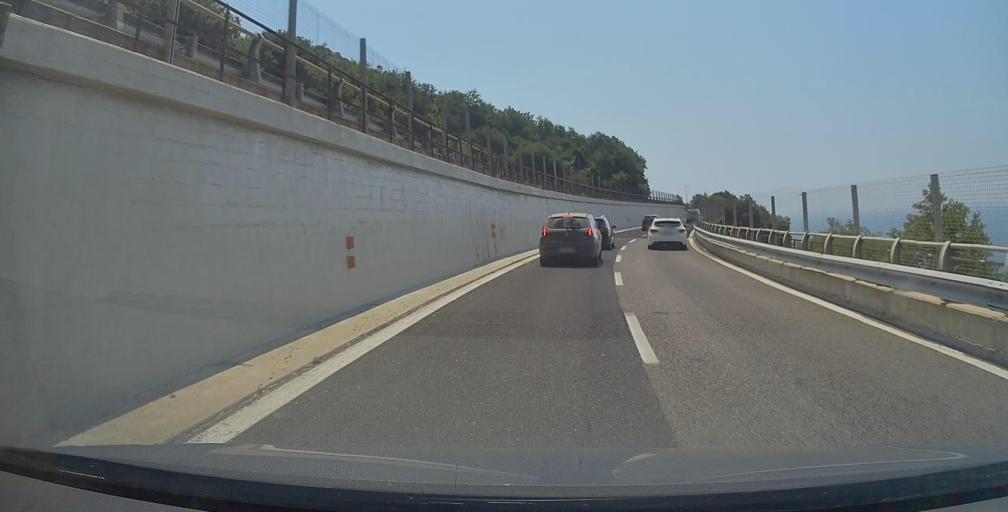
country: IT
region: Campania
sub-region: Provincia di Salerno
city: Vietri sul Mare
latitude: 40.6747
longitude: 14.7294
